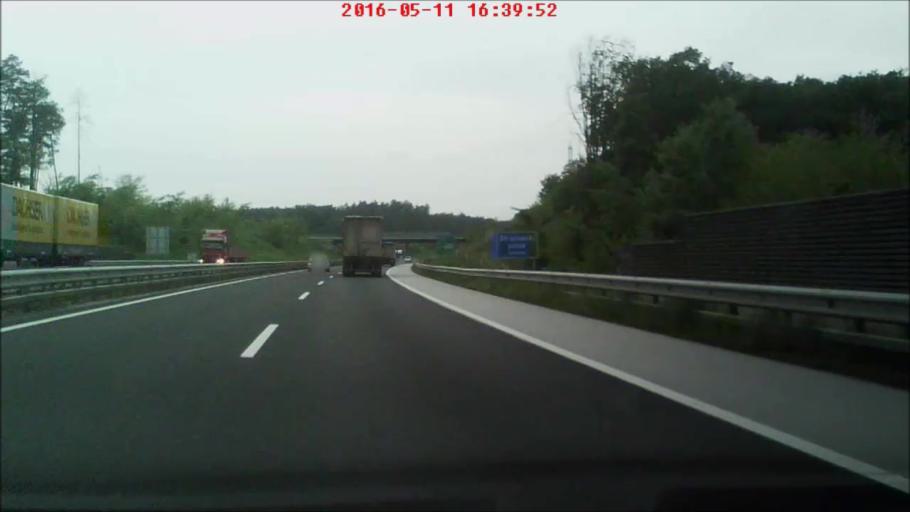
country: SI
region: Miklavz na Dravskem Polju
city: Miklavz na Dravskem Polju
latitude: 46.5281
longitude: 15.6980
